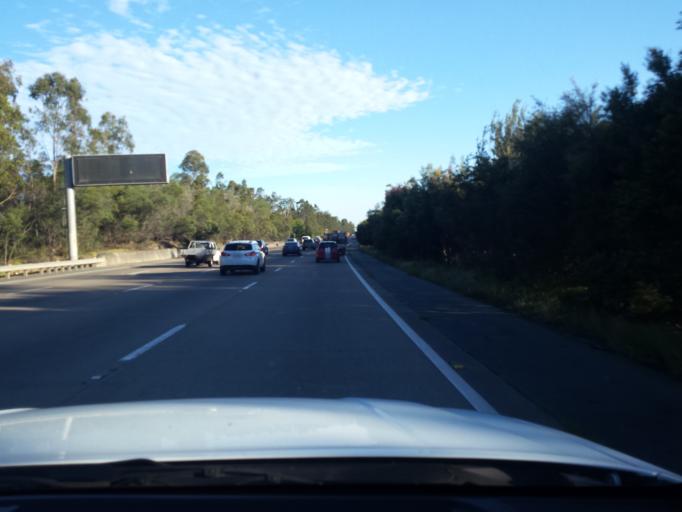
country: AU
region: Queensland
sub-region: Gold Coast
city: Ormeau Hills
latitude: -27.8323
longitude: 153.3017
